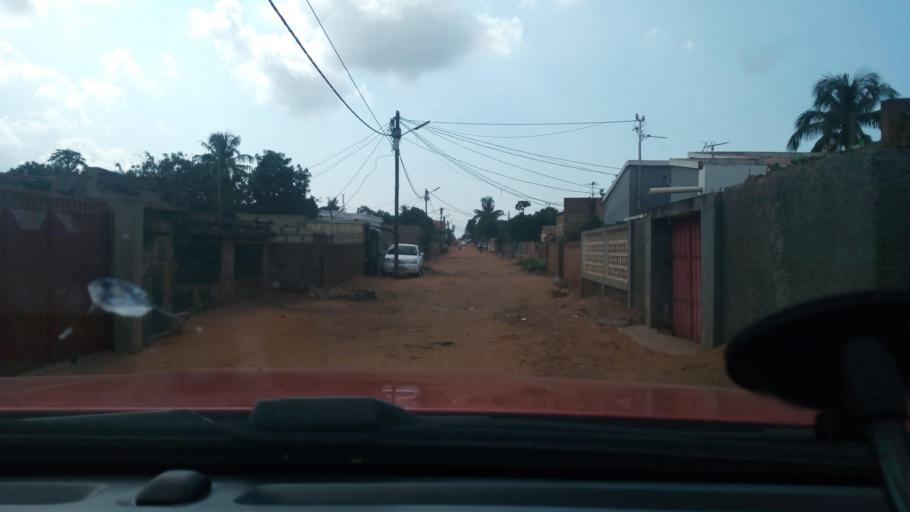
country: MZ
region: Maputo City
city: Maputo
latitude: -25.9226
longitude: 32.5902
